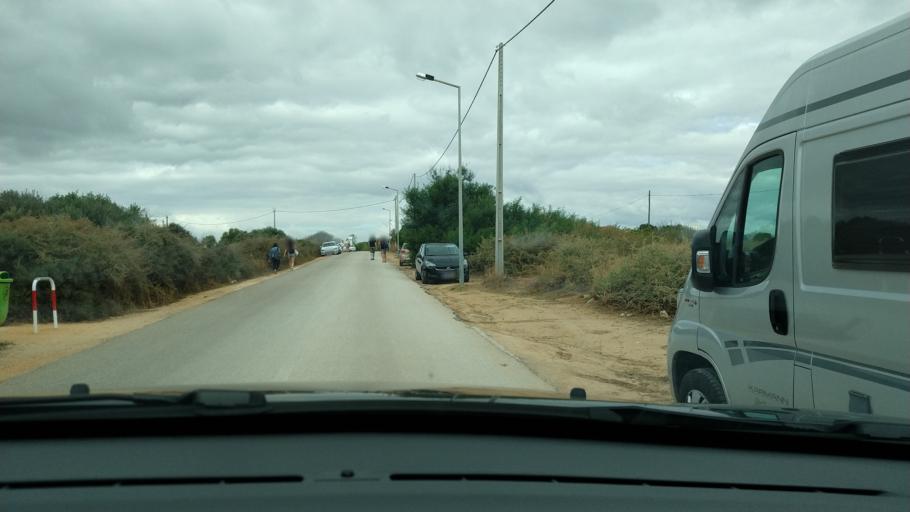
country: PT
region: Faro
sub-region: Lagos
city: Lagos
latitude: 37.0827
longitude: -8.6701
